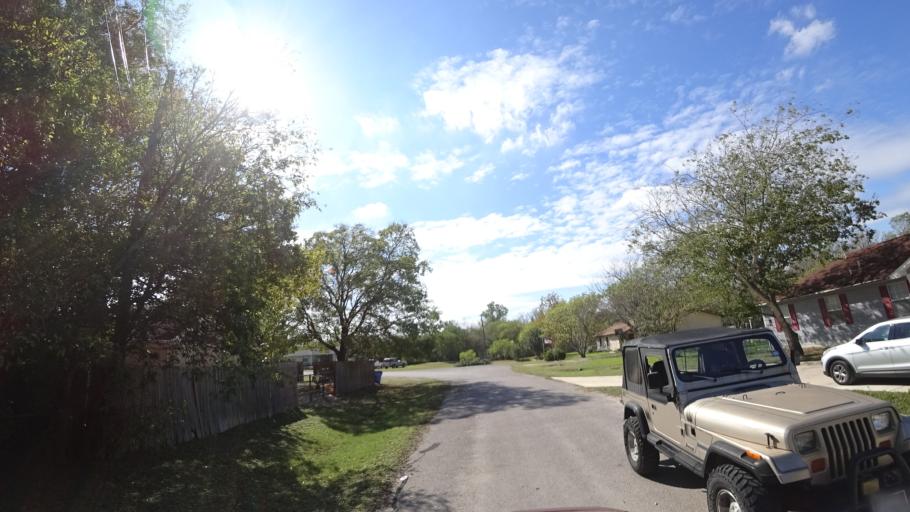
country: US
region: Texas
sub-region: Travis County
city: Windemere
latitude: 30.4519
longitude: -97.6417
